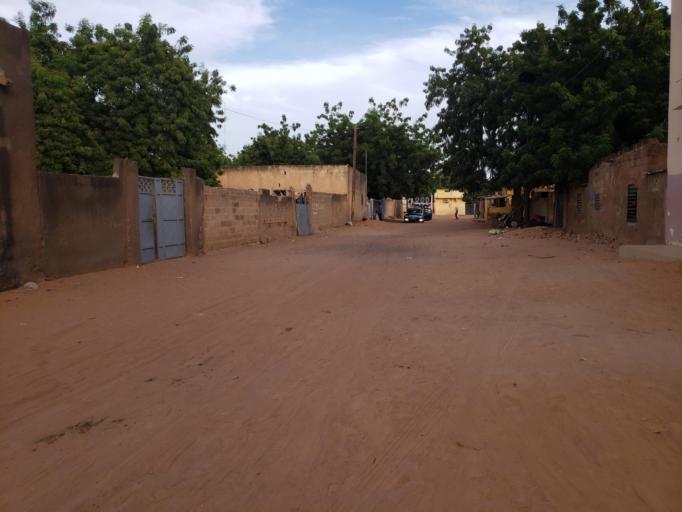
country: SN
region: Louga
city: Ndibene Dahra
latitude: 15.3947
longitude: -15.1198
